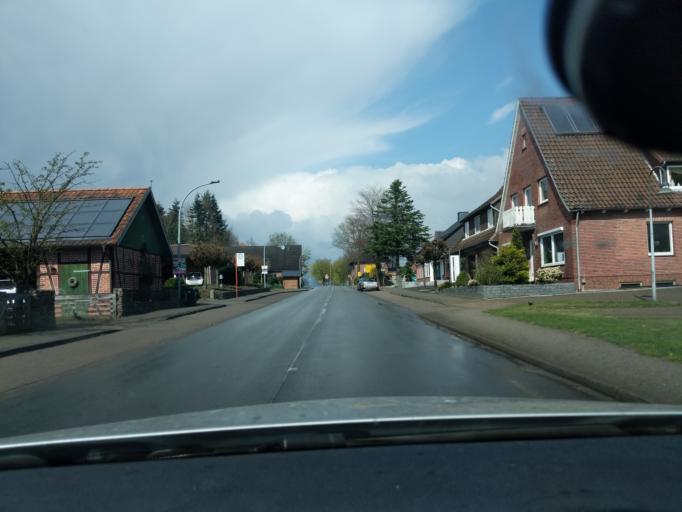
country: DE
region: Lower Saxony
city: Bargstedt
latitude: 53.4599
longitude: 9.4458
